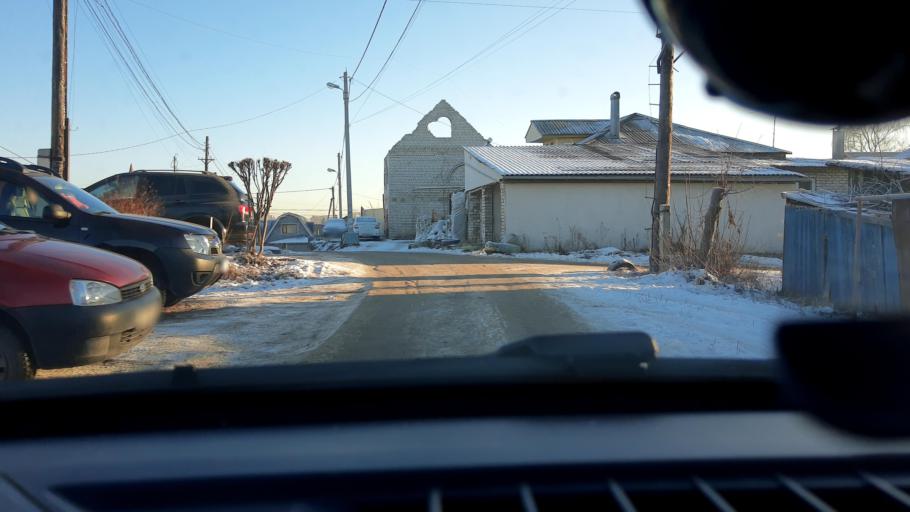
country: RU
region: Nizjnij Novgorod
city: Gorbatovka
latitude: 56.3329
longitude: 43.8247
